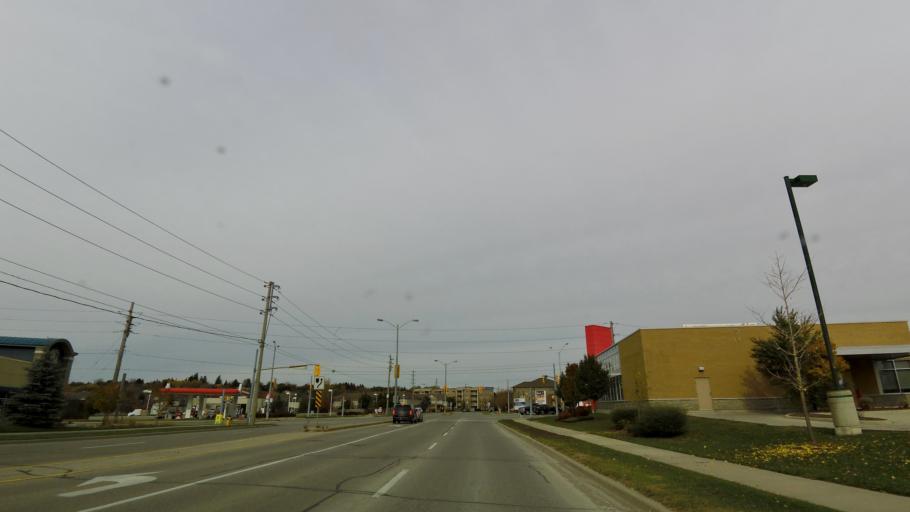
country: CA
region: Ontario
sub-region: Wellington County
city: Guelph
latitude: 43.5245
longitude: -80.2858
